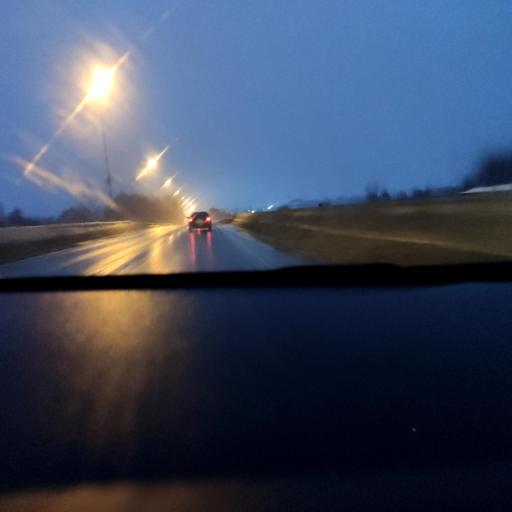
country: RU
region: Tatarstan
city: Stolbishchi
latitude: 55.6047
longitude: 49.4293
